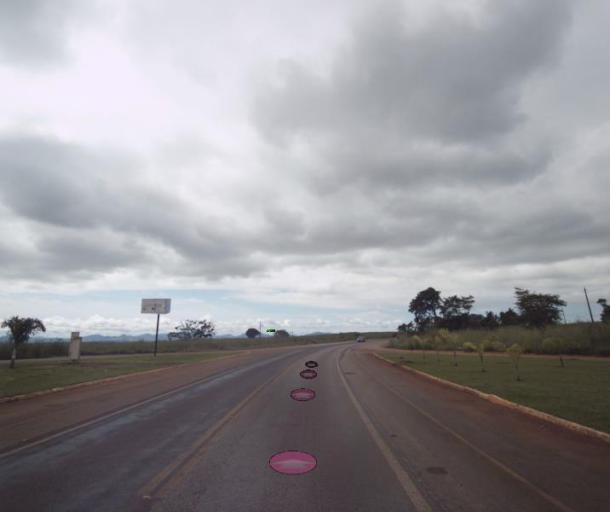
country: BR
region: Goias
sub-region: Barro Alto
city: Barro Alto
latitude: -14.9887
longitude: -48.9100
